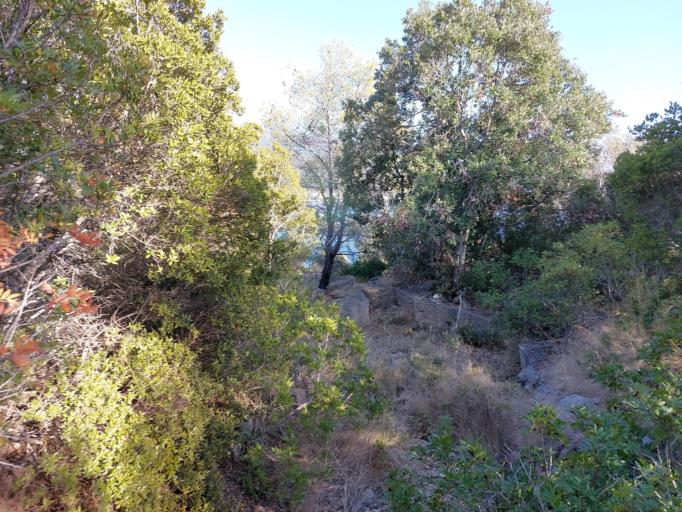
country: HR
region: Dubrovacko-Neretvanska
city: Smokvica
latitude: 42.7555
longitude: 16.8135
